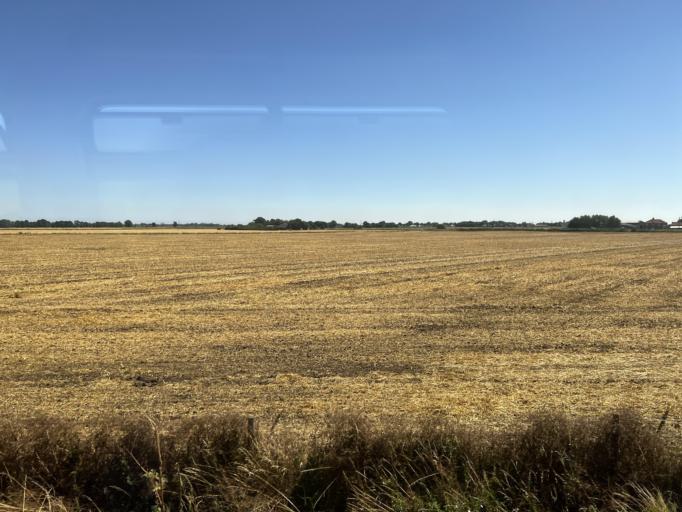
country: GB
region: England
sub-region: Lincolnshire
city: Spilsby
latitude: 53.0937
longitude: 0.1021
